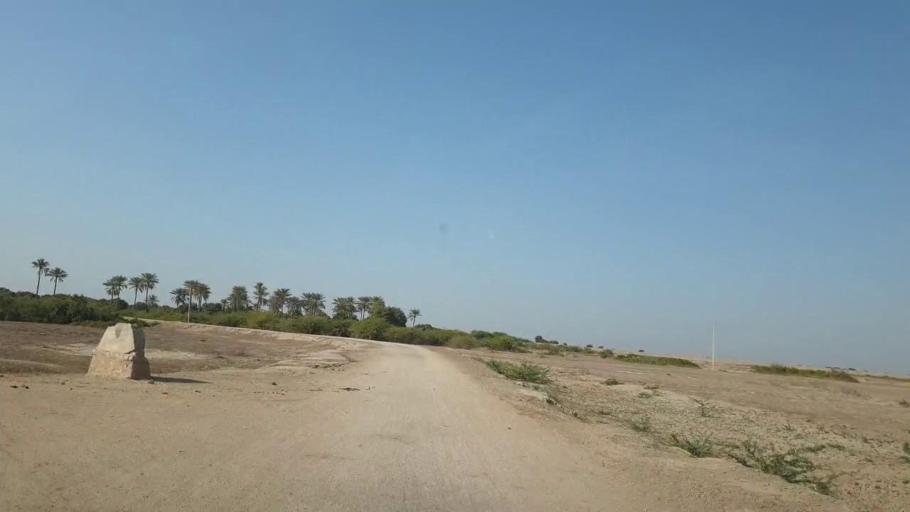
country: PK
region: Sindh
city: Nabisar
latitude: 25.0223
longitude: 69.4733
